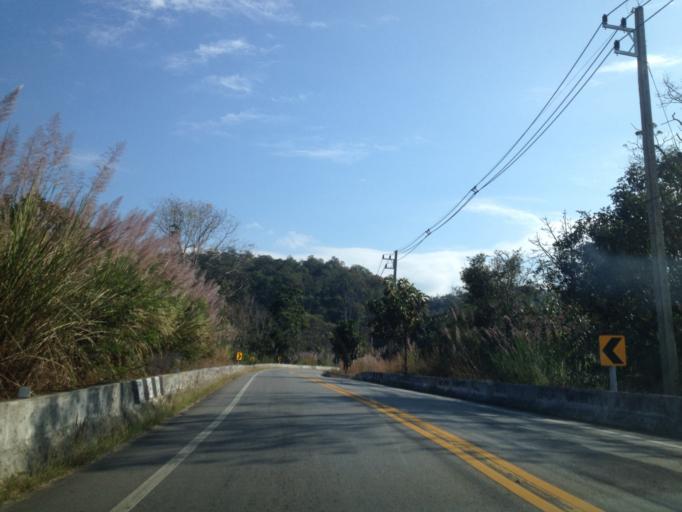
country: TH
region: Mae Hong Son
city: Ban Huai I Huak
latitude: 18.1481
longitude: 98.2595
